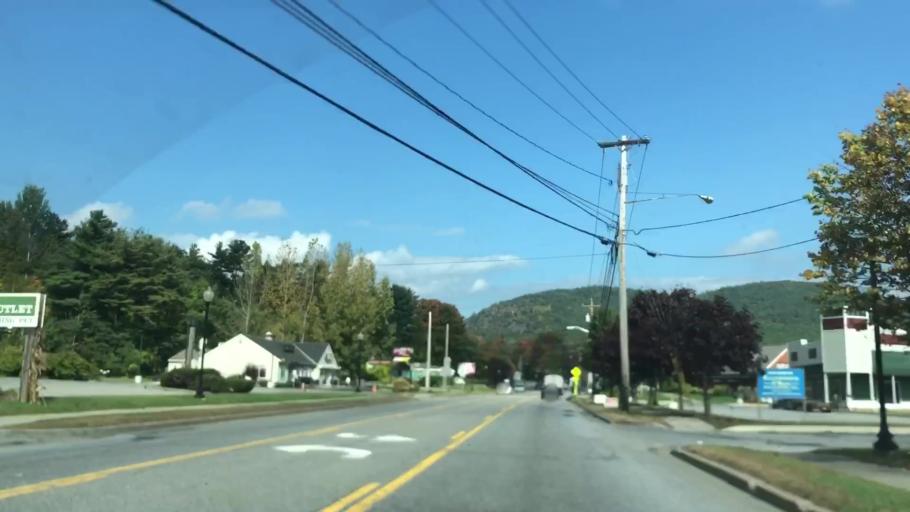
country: US
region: New York
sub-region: Warren County
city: Glens Falls North
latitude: 43.3665
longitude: -73.6994
